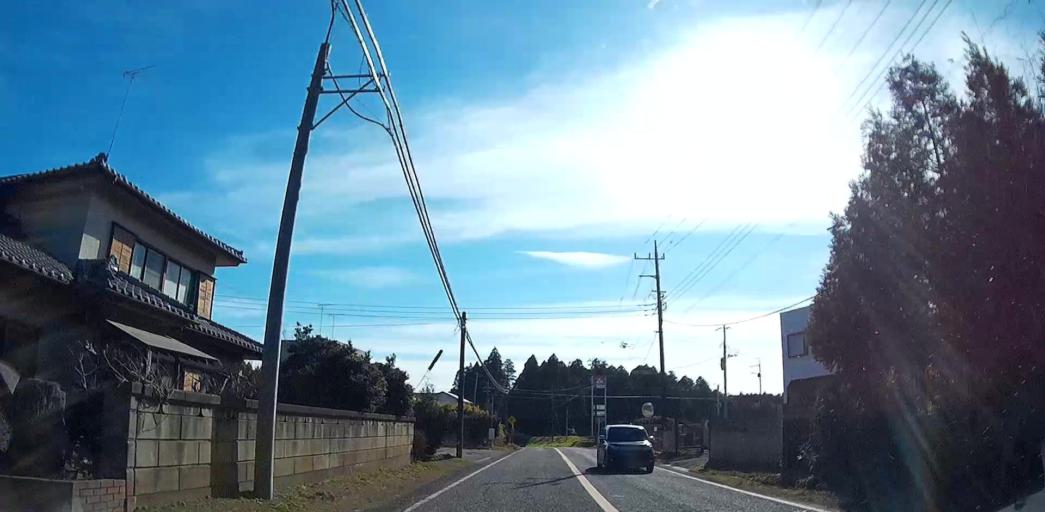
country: JP
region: Chiba
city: Yokaichiba
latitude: 35.7648
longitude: 140.4456
